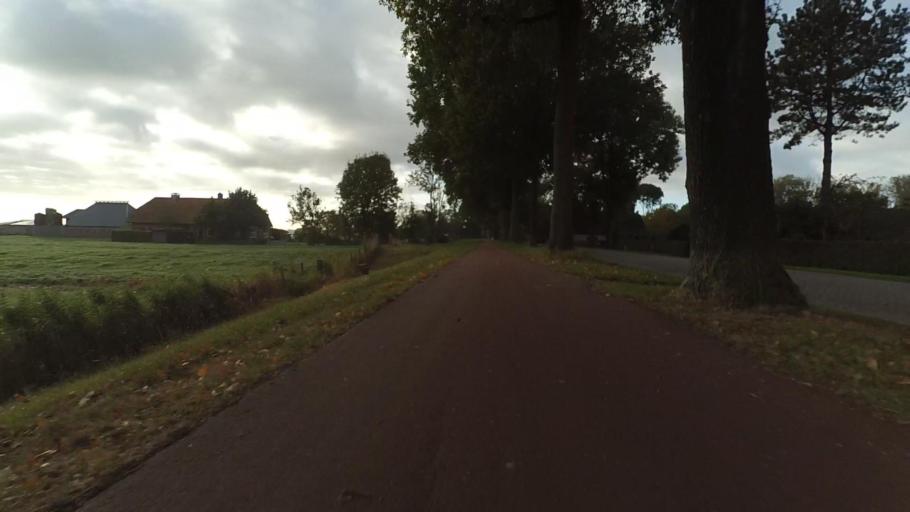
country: NL
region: North Holland
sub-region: Gemeente Blaricum
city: Blaricum
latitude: 52.2551
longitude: 5.2682
